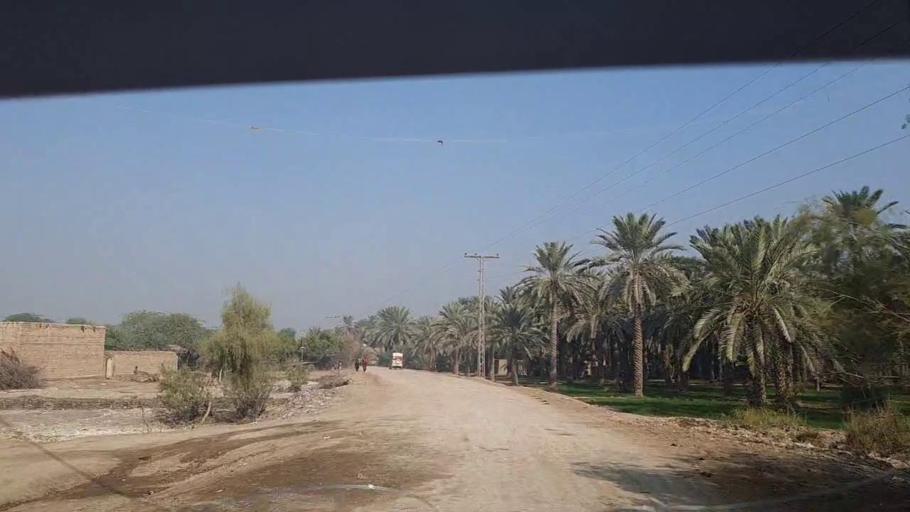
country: PK
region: Sindh
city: Khairpur
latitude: 27.4976
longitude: 68.7371
